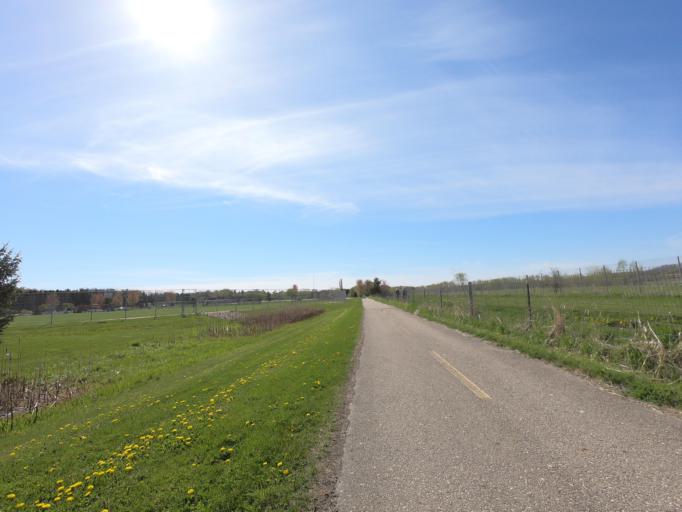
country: US
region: Wisconsin
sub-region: Dane County
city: Middleton
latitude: 43.1128
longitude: -89.5383
